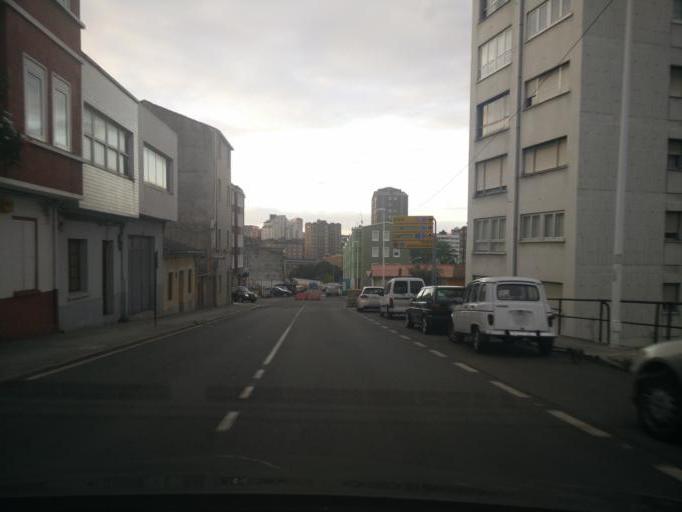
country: ES
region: Galicia
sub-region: Provincia da Coruna
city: A Coruna
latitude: 43.3423
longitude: -8.4152
